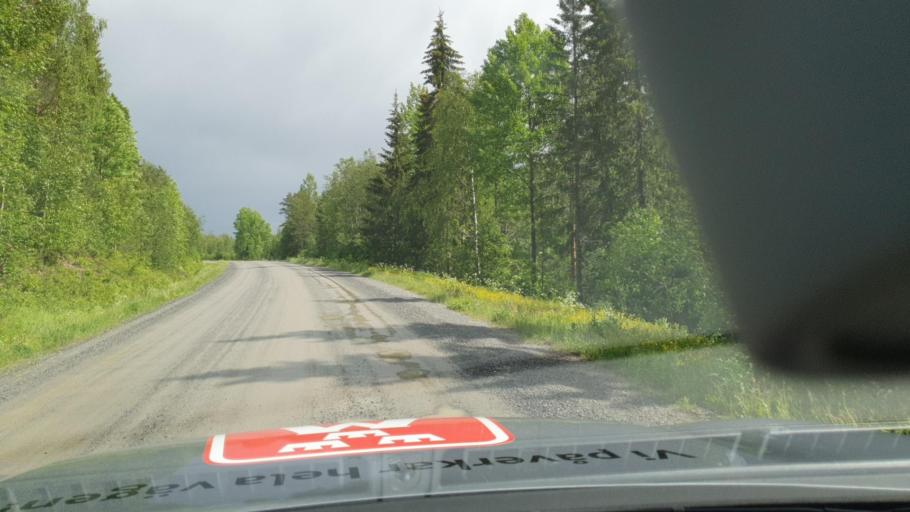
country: SE
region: Vaesternorrland
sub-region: Kramfors Kommun
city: Bollstabruk
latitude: 63.3852
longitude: 17.7130
